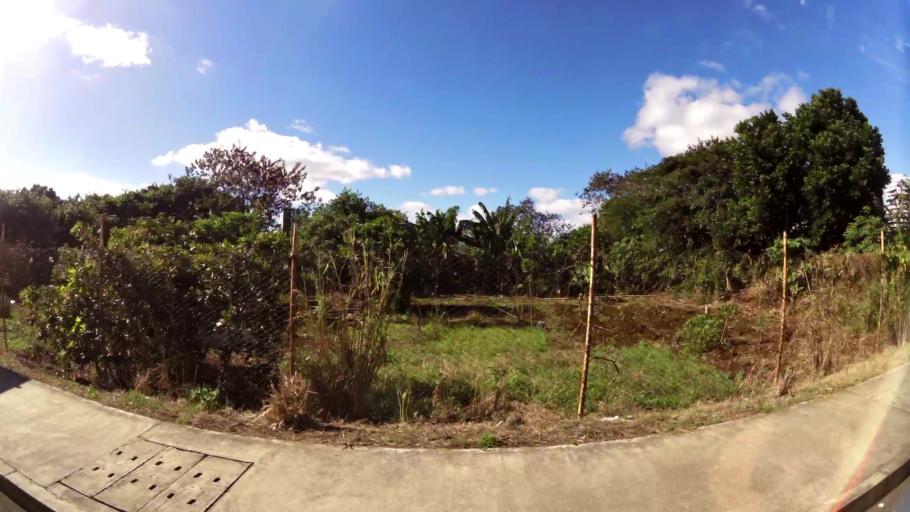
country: MU
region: Plaines Wilhems
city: Quatre Bornes
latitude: -20.2619
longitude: 57.4889
